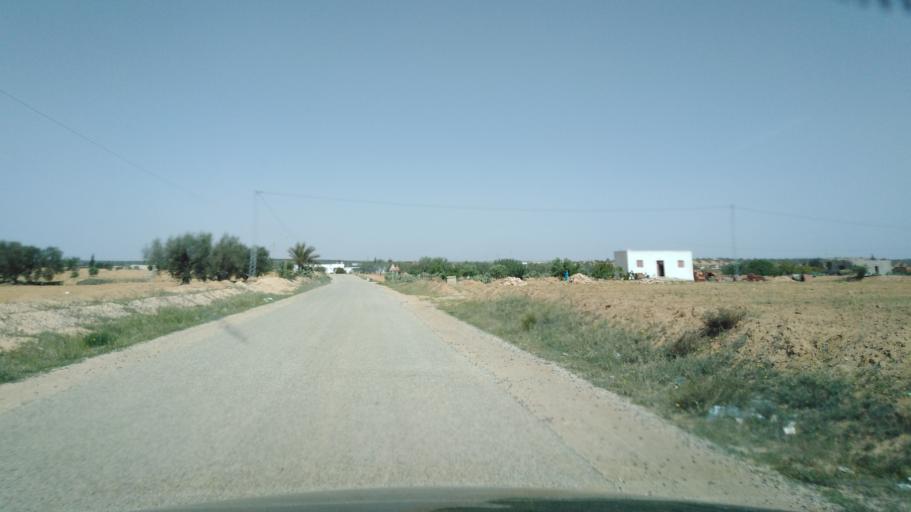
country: TN
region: Safaqis
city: Sfax
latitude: 34.6783
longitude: 10.4385
